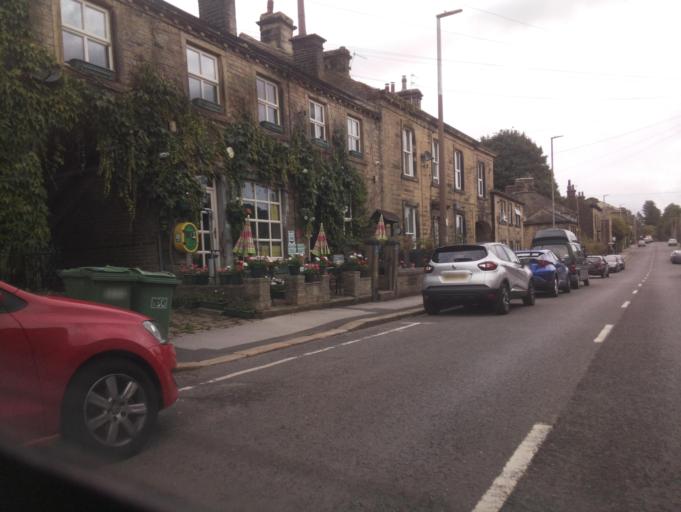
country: GB
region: England
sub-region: Kirklees
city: Holmfirth
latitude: 53.5601
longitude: -1.8120
